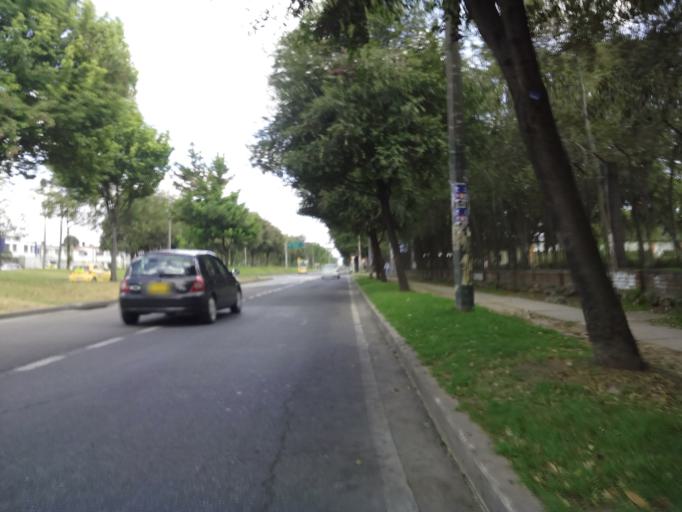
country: CO
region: Bogota D.C.
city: Bogota
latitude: 4.6639
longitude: -74.1082
